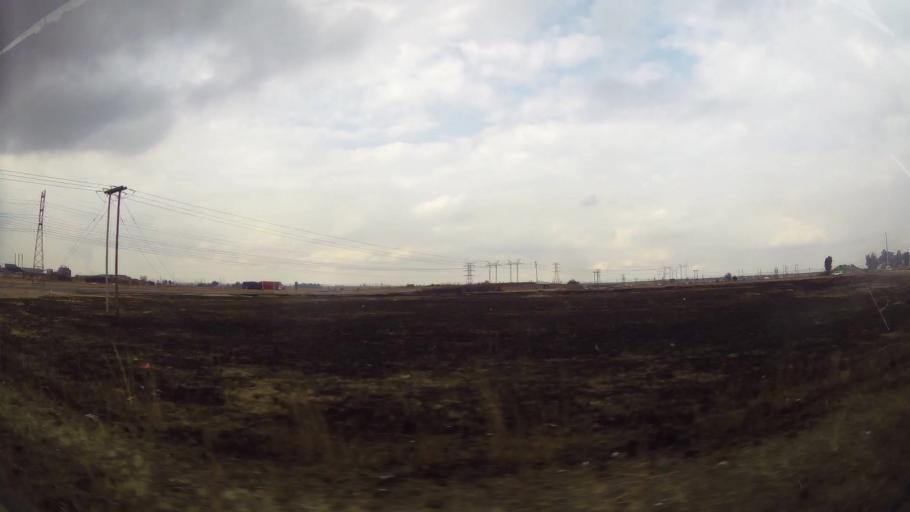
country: ZA
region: Orange Free State
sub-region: Fezile Dabi District Municipality
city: Sasolburg
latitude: -26.8390
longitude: 27.8714
